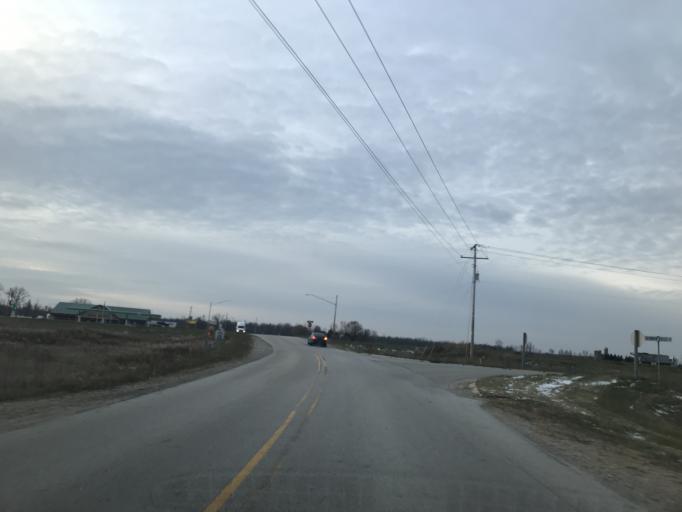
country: US
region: Wisconsin
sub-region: Marinette County
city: Peshtigo
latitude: 45.0521
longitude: -87.8001
